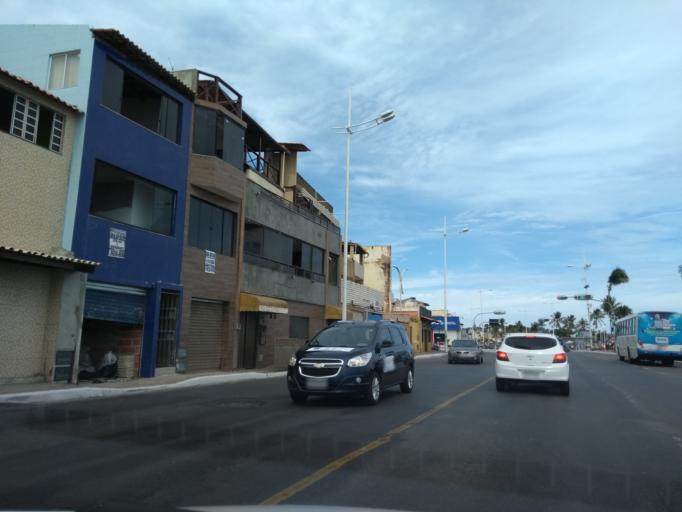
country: BR
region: Bahia
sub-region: Lauro De Freitas
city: Lauro de Freitas
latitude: -12.9505
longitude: -38.3684
